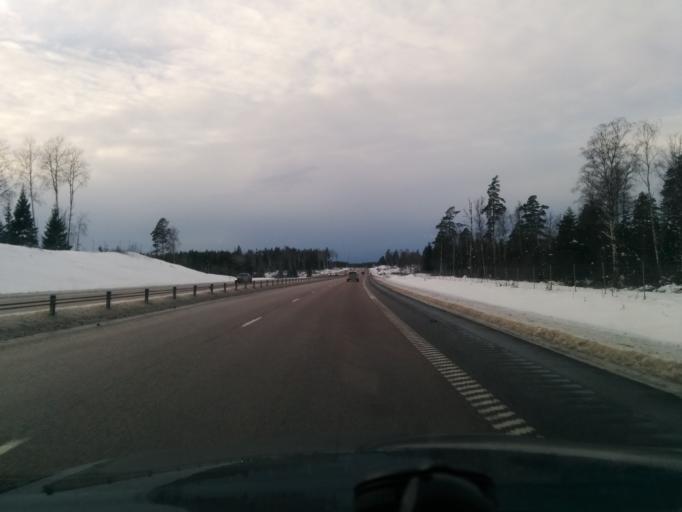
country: SE
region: Uppsala
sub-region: Enkopings Kommun
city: Hummelsta
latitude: 59.6390
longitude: 16.9366
